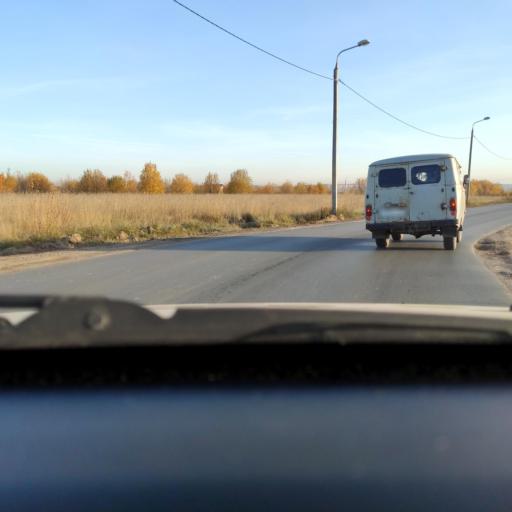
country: RU
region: Perm
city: Perm
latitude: 58.0175
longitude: 56.3353
